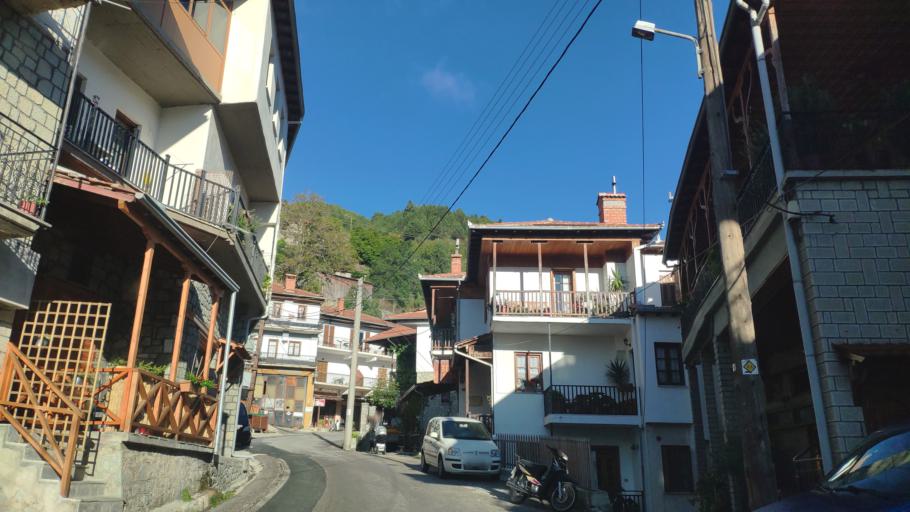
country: GR
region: Epirus
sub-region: Nomos Ioanninon
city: Metsovo
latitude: 39.7728
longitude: 21.1806
